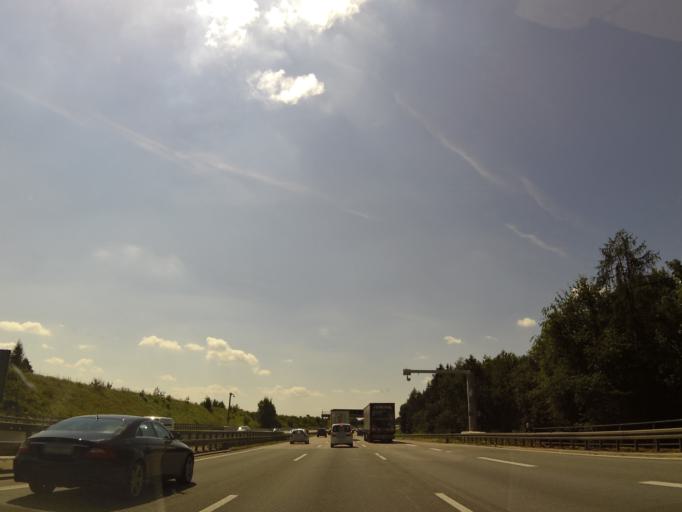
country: DE
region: Bavaria
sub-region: Upper Bavaria
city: Schweitenkirchen
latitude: 48.5505
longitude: 11.5918
